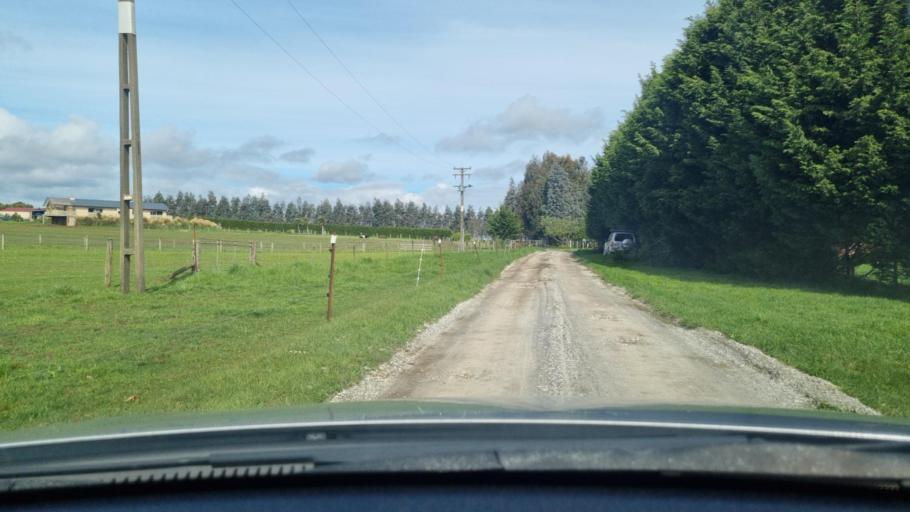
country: NZ
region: Southland
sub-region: Invercargill City
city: Invercargill
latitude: -46.4537
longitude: 168.3788
